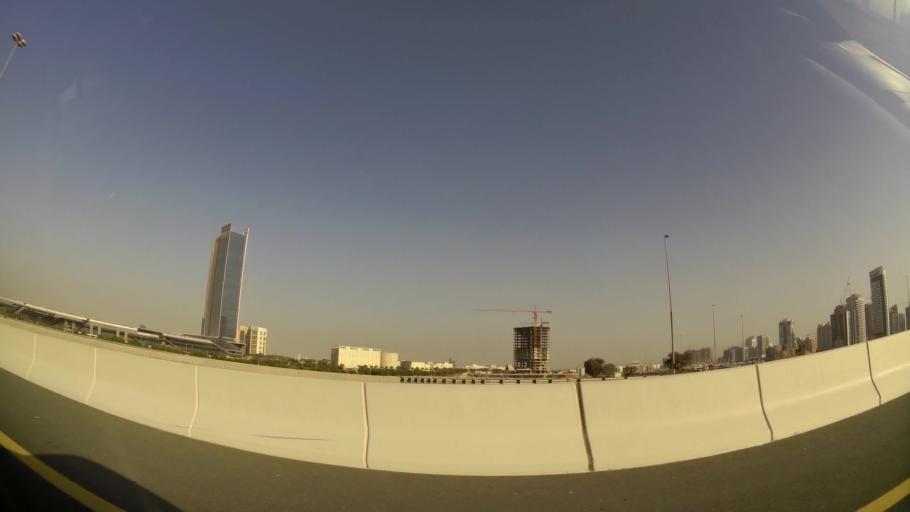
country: AE
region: Dubai
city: Dubai
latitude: 25.0495
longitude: 55.2255
